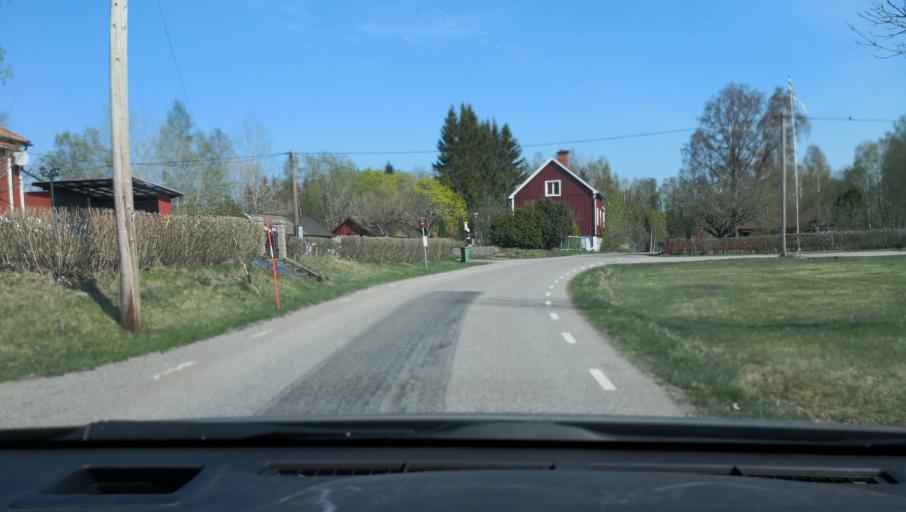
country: SE
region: Uppsala
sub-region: Heby Kommun
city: Heby
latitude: 60.0352
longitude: 16.8074
